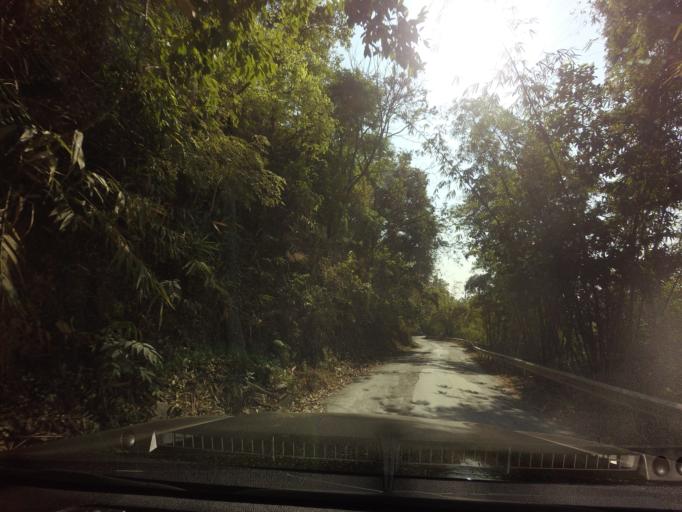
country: TH
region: Kanchanaburi
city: Thong Pha Phum
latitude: 14.7014
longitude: 98.4600
